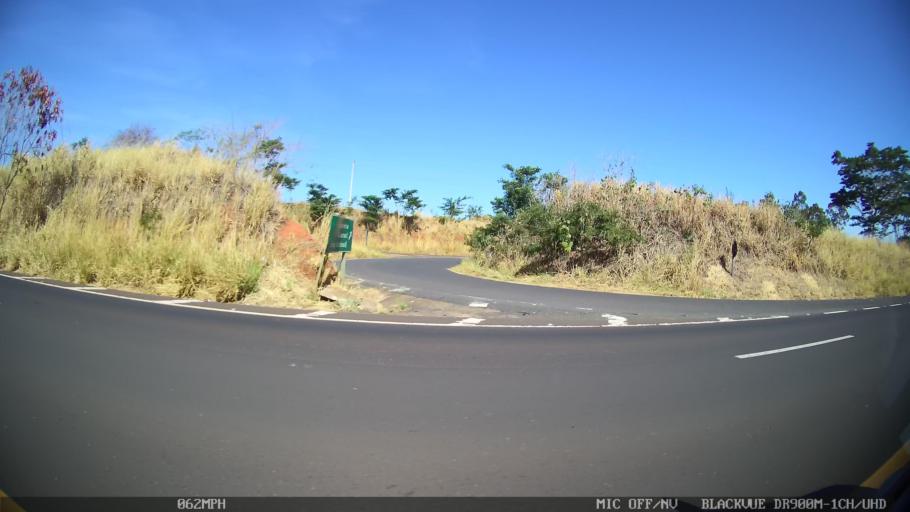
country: BR
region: Sao Paulo
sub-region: Barretos
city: Barretos
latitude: -20.6101
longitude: -48.7508
